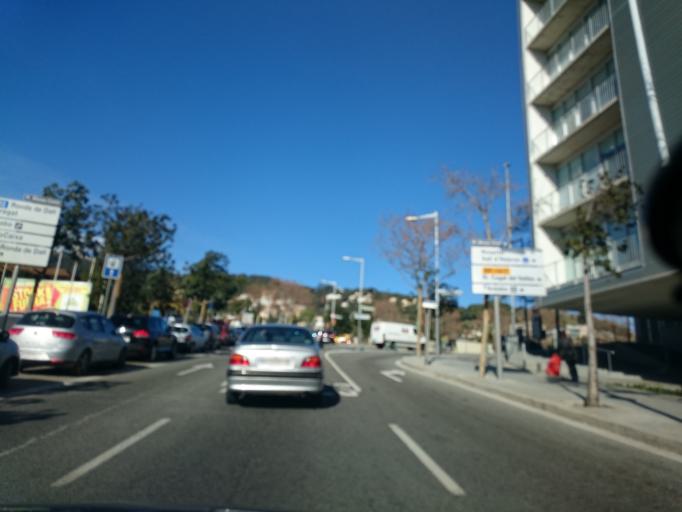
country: ES
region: Catalonia
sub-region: Provincia de Barcelona
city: Sarria-Sant Gervasi
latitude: 41.4155
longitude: 2.1380
